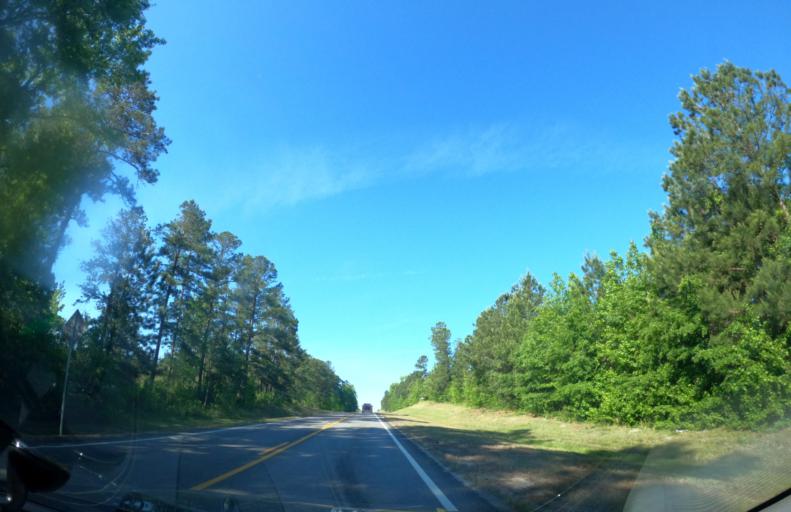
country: US
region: Georgia
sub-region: Columbia County
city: Harlem
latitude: 33.3347
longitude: -82.3605
